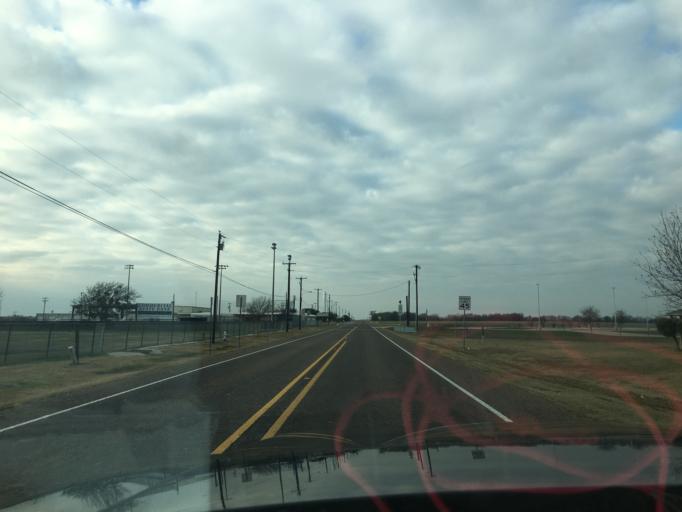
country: US
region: Texas
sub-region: Ellis County
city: Palmer
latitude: 32.4293
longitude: -96.6794
